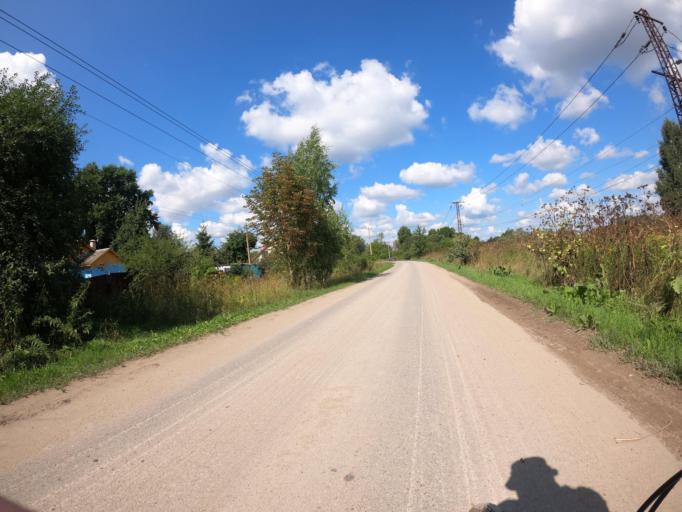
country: RU
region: Moskovskaya
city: Lopatinskiy
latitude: 55.3140
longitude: 38.7060
